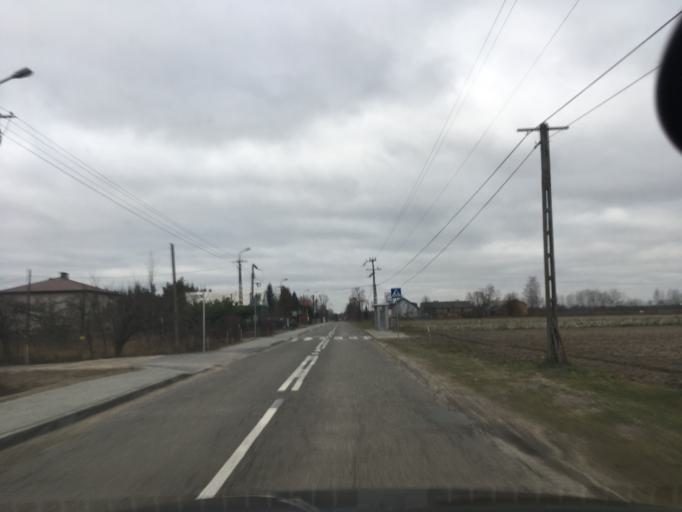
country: PL
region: Masovian Voivodeship
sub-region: Powiat piaseczynski
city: Lesznowola
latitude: 52.0445
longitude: 20.9518
